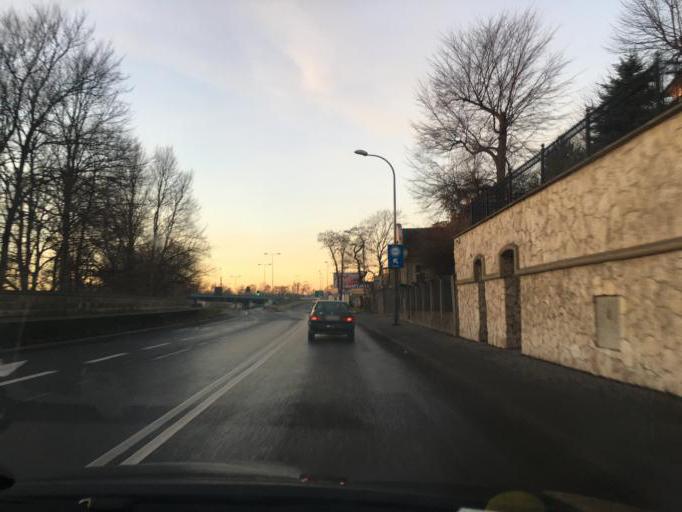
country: PL
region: Lesser Poland Voivodeship
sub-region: Krakow
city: Krakow
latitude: 50.0506
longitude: 19.9072
